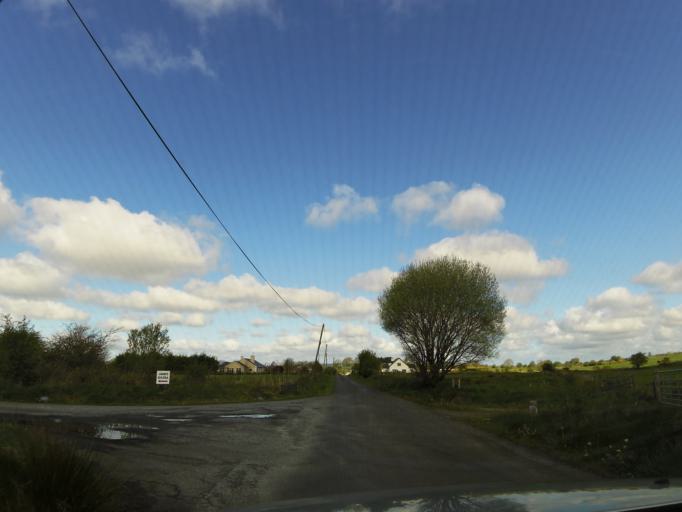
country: IE
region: Connaught
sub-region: Maigh Eo
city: Kiltamagh
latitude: 53.7877
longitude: -8.9400
